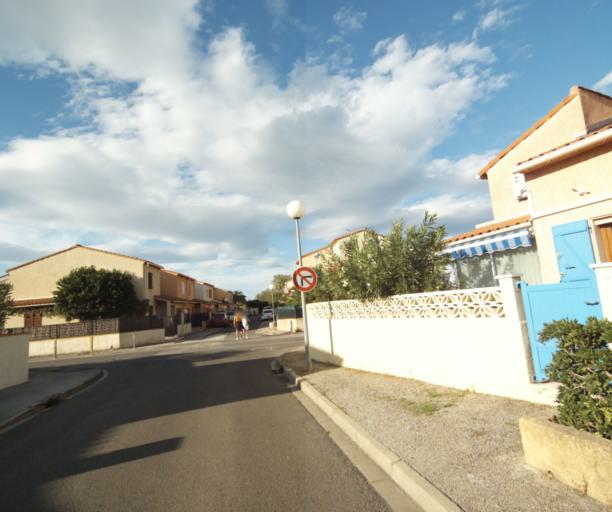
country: FR
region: Languedoc-Roussillon
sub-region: Departement des Pyrenees-Orientales
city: Argelers
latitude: 42.5500
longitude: 3.0393
